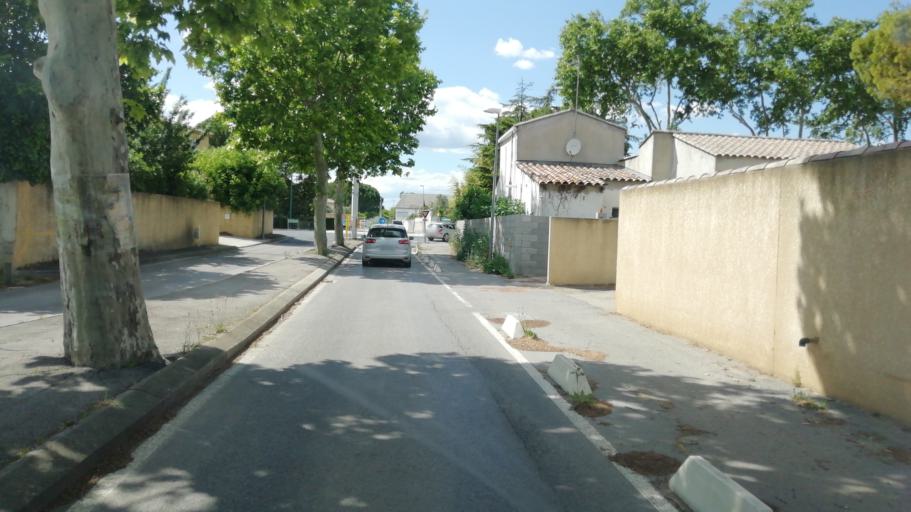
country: FR
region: Languedoc-Roussillon
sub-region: Departement de l'Herault
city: Saint-Just
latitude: 43.6582
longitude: 4.1162
